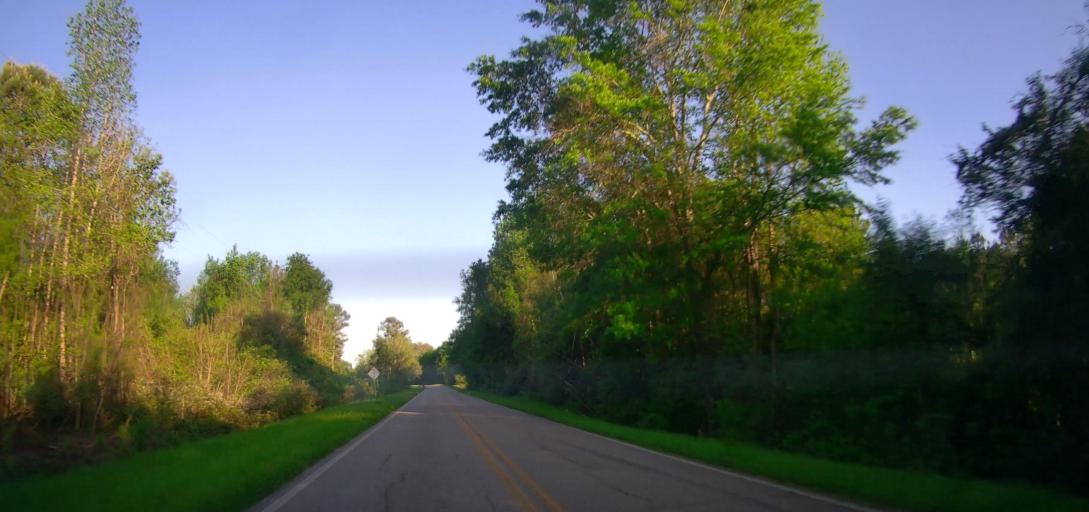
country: US
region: Georgia
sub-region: Macon County
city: Oglethorpe
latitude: 32.3036
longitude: -84.1040
